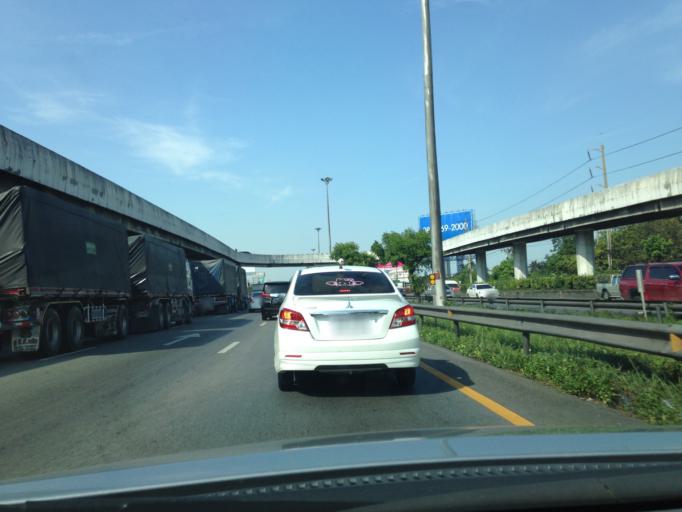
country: TH
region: Nonthaburi
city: Bang Yai
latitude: 13.8591
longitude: 100.4113
